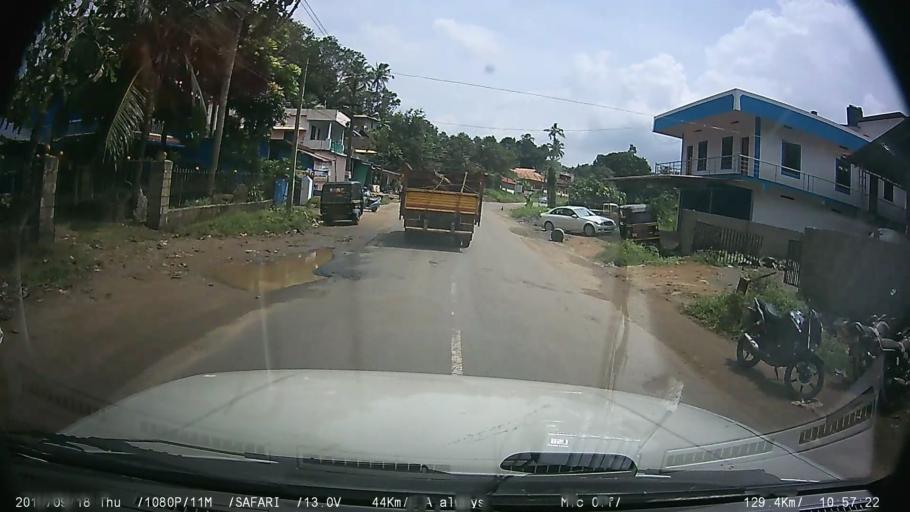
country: IN
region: Kerala
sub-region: Ernakulam
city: Piravam
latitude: 9.8478
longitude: 76.5914
